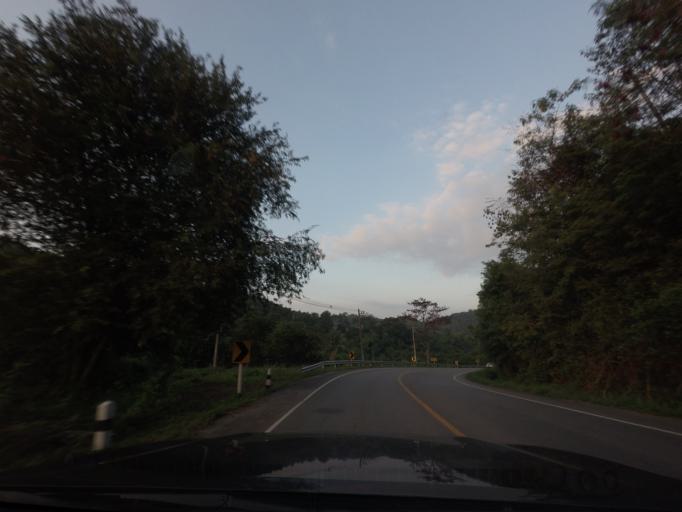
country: TH
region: Nan
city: Na Noi
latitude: 18.3837
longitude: 100.7090
